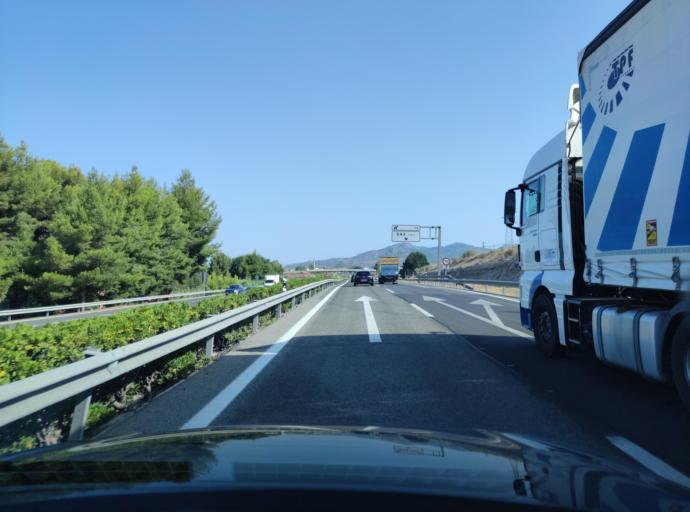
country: ES
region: Valencia
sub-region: Provincia de Alicante
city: Sax
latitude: 38.5338
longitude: -0.8083
